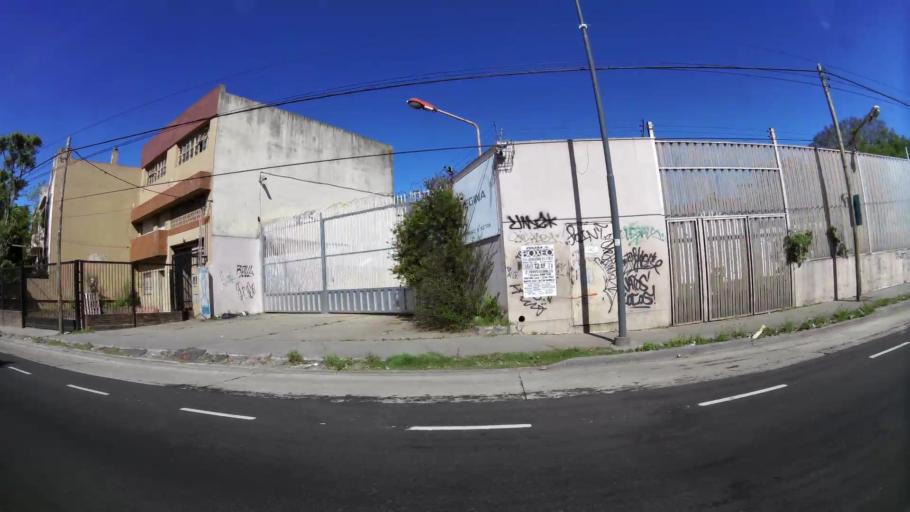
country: AR
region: Buenos Aires
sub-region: Partido de General San Martin
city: General San Martin
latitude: -34.5236
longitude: -58.5714
